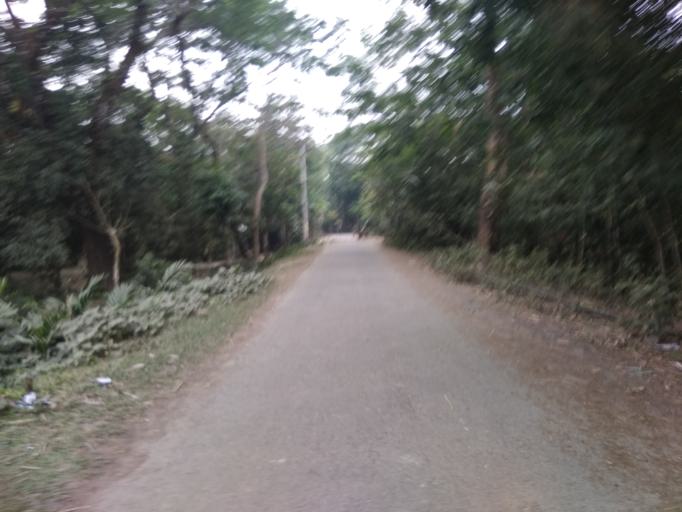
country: BD
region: Barisal
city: Mehendiganj
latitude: 22.9209
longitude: 90.3914
